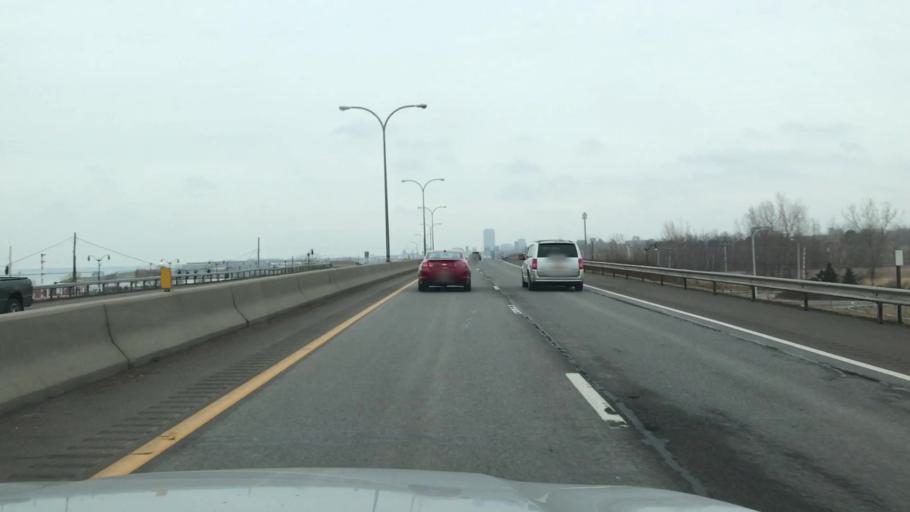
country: US
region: New York
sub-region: Erie County
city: Lackawanna
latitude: 42.8383
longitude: -78.8562
